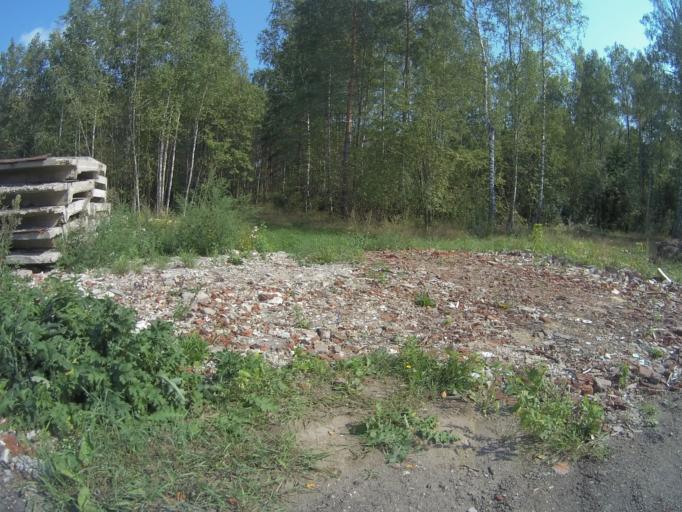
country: RU
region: Vladimir
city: Raduzhnyy
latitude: 55.9943
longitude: 40.2926
